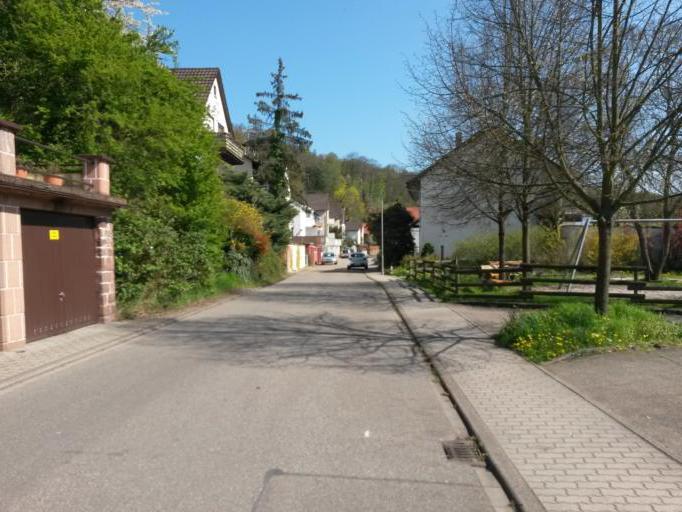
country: DE
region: Baden-Wuerttemberg
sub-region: Karlsruhe Region
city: Joehlingen
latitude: 48.9839
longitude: 8.5501
